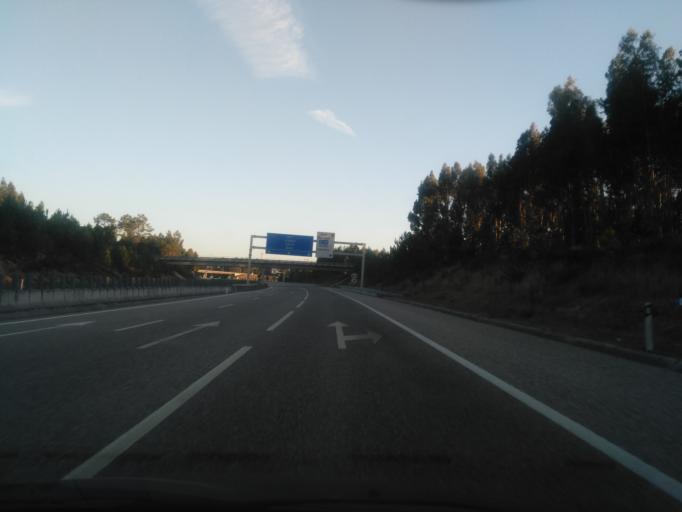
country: PT
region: Leiria
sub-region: Pombal
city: Lourical
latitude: 39.9944
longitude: -8.7982
